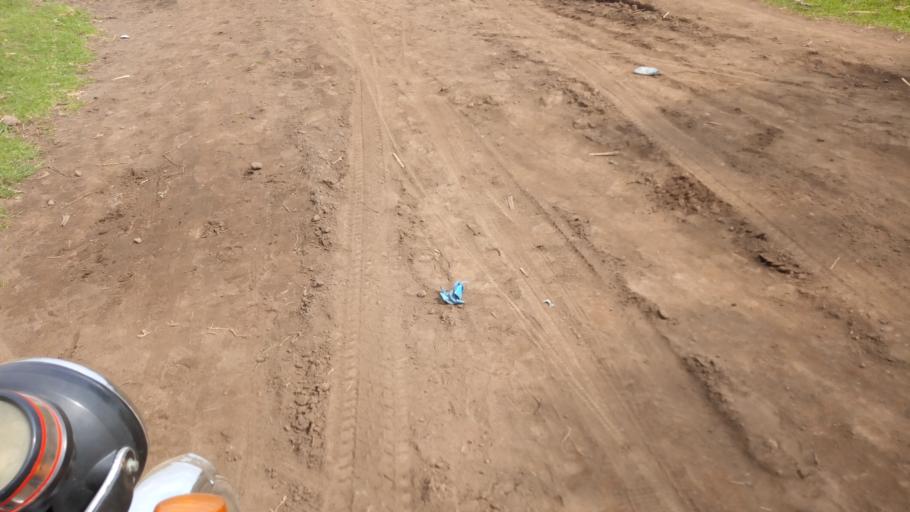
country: UG
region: Western Region
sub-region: Kisoro District
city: Kisoro
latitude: -1.3326
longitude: 29.6133
